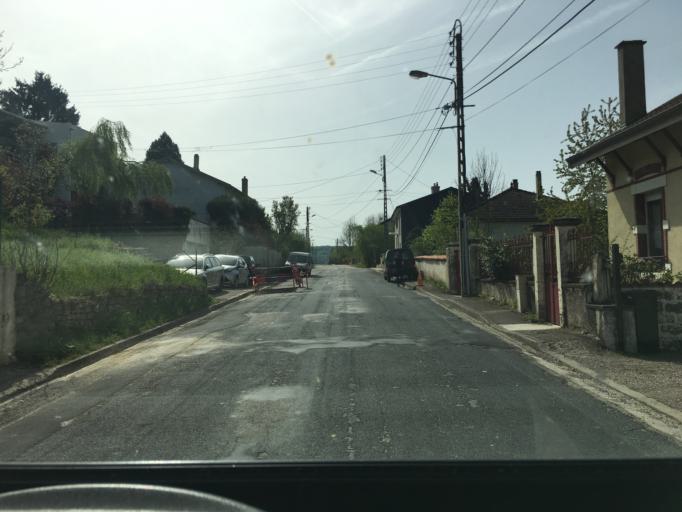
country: FR
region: Lorraine
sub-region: Departement de Meurthe-et-Moselle
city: Chaligny
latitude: 48.6337
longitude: 6.0473
